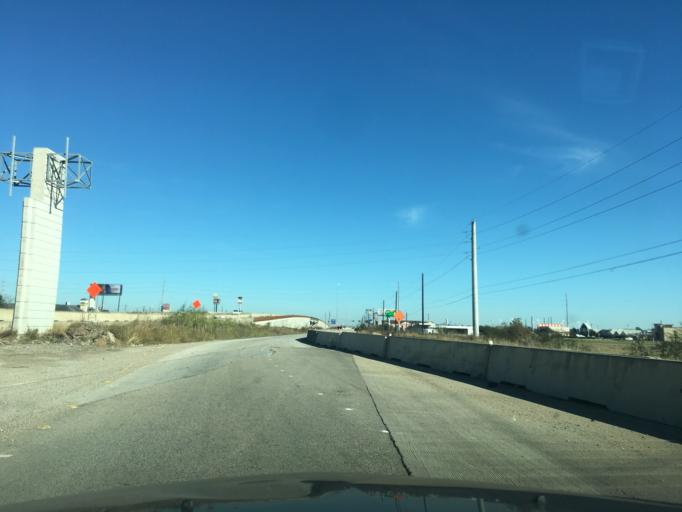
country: US
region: Texas
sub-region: Fort Bend County
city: Rosenberg
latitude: 29.5316
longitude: -95.8123
